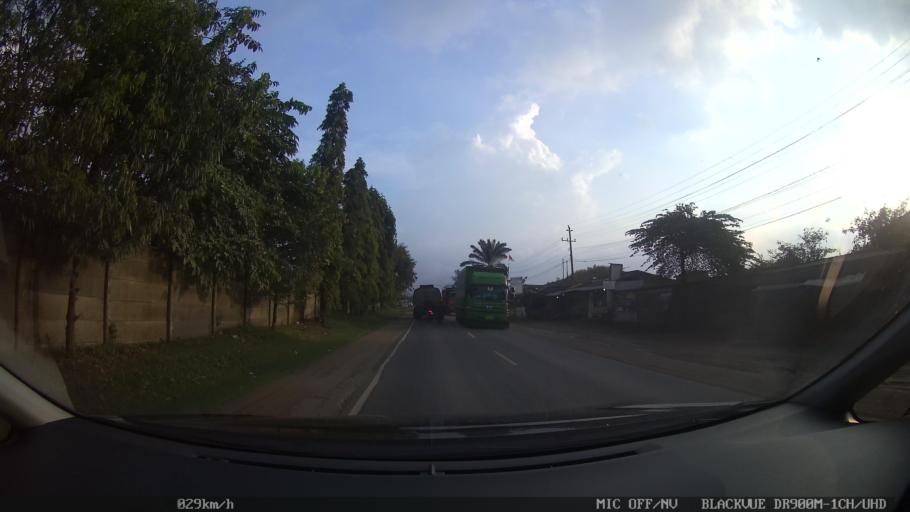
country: ID
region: Lampung
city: Panjang
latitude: -5.4109
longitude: 105.3470
